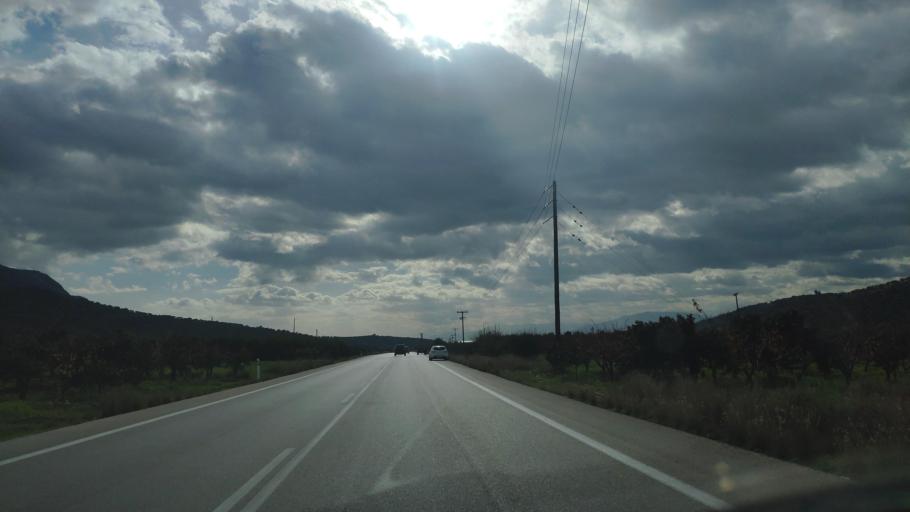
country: GR
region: Peloponnese
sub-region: Nomos Argolidos
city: Koutsopodi
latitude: 37.7452
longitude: 22.7371
